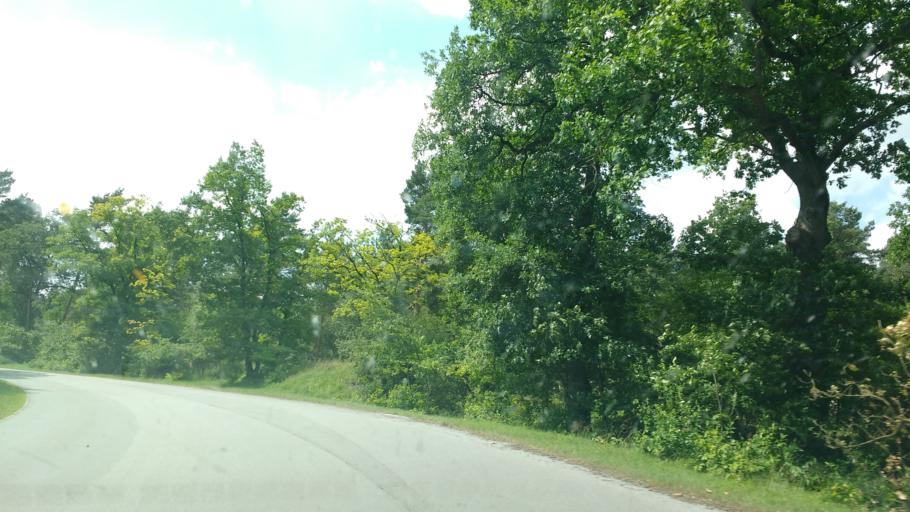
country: DE
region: North Rhine-Westphalia
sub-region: Regierungsbezirk Detmold
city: Paderborn
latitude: 51.7766
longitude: 8.7501
